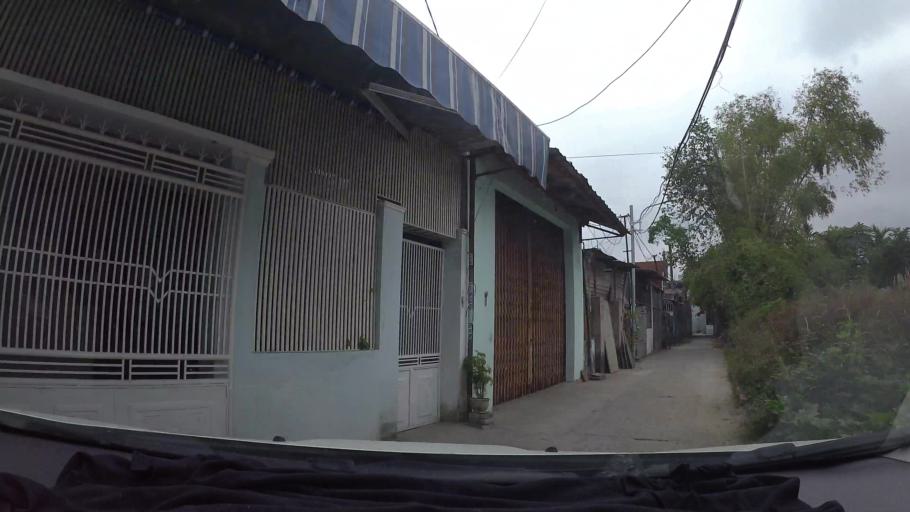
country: VN
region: Da Nang
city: Lien Chieu
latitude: 16.0662
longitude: 108.1688
